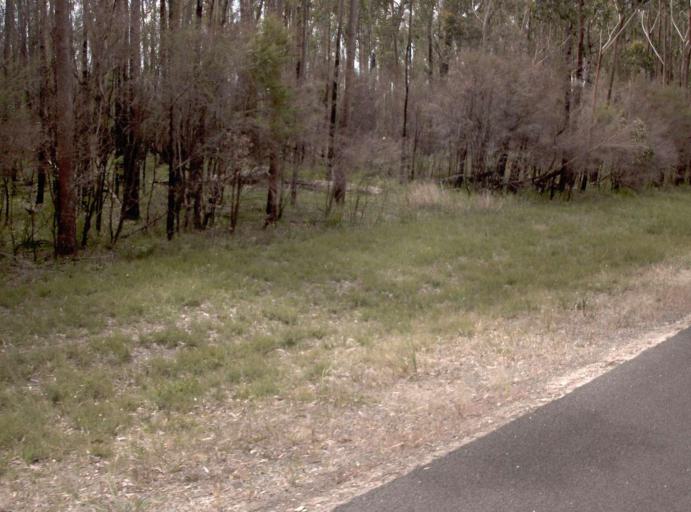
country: AU
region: New South Wales
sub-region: Bega Valley
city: Eden
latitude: -37.5214
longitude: 149.4949
